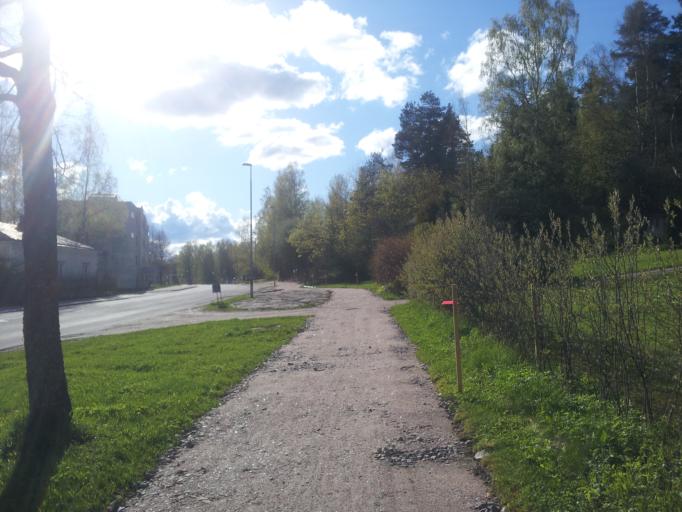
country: FI
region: Haeme
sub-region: Riihimaeki
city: Riihimaeki
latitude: 60.7475
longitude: 24.7723
